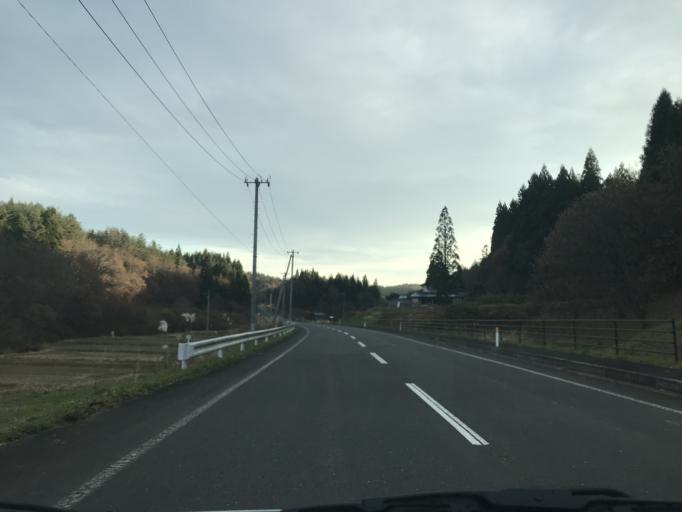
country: JP
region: Iwate
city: Ichinoseki
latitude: 38.9917
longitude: 141.0661
